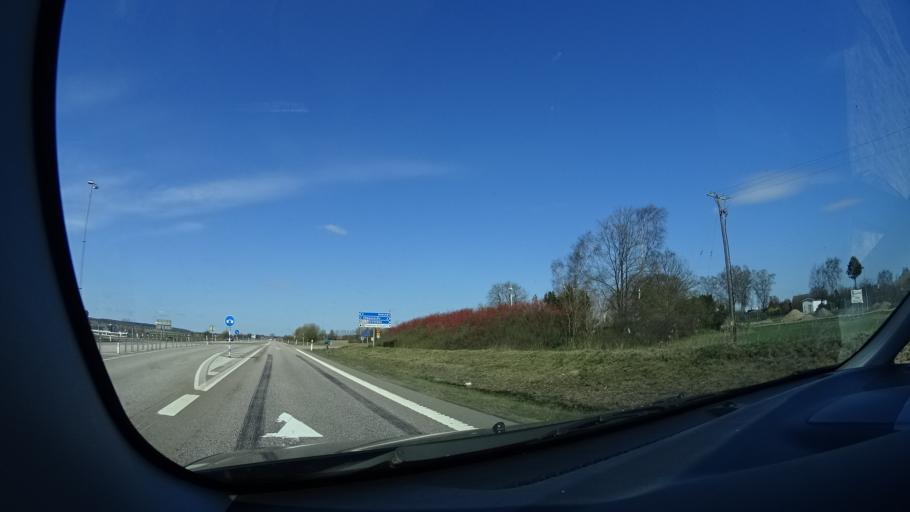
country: SE
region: Skane
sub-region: Astorps Kommun
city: Kvidinge
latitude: 56.1286
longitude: 13.0575
